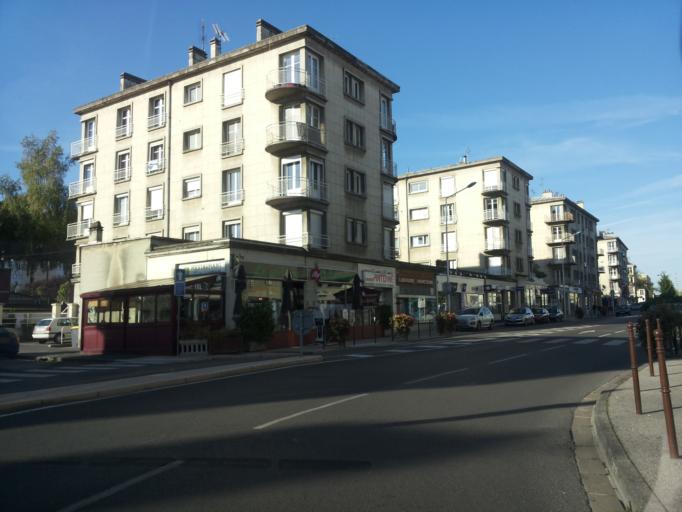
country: FR
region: Picardie
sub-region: Departement de l'Aisne
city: Laon
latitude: 49.5698
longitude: 3.6262
